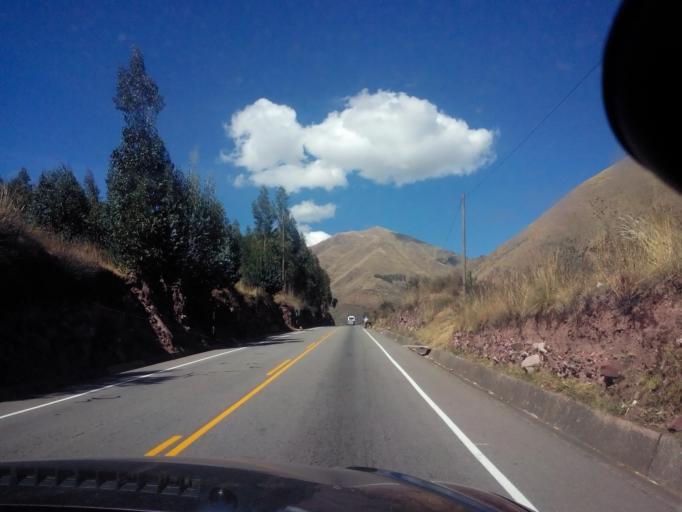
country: PE
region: Cusco
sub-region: Provincia de Quispicanchis
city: Cusipata
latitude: -13.9645
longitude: -71.4953
